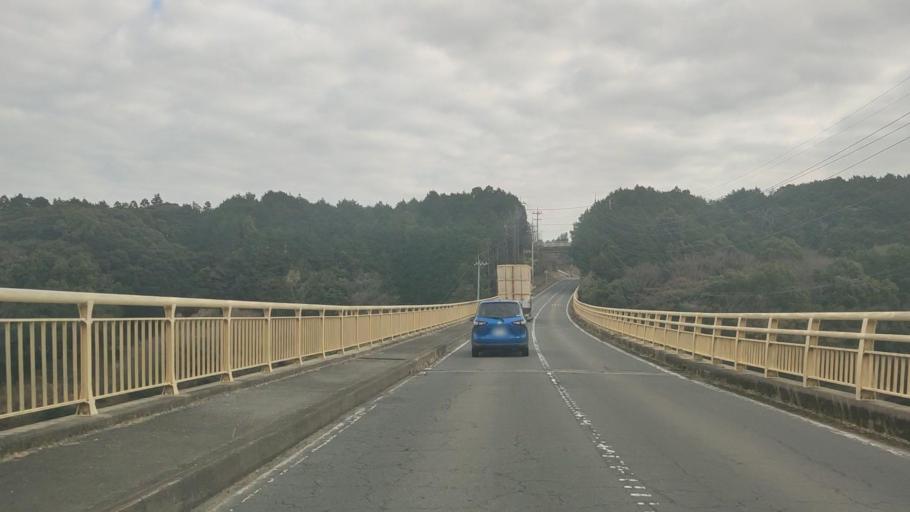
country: JP
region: Nagasaki
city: Shimabara
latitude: 32.8490
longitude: 130.2253
